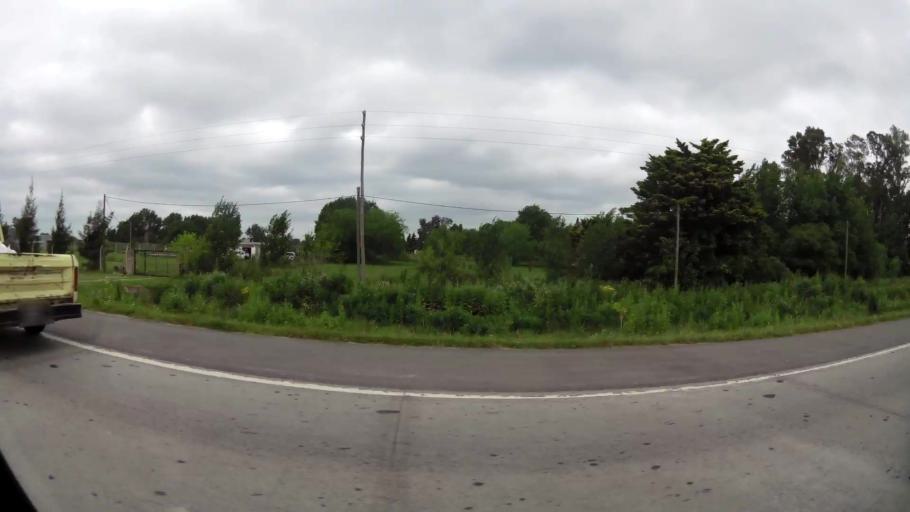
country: AR
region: Buenos Aires
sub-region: Partido de San Vicente
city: San Vicente
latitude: -35.0471
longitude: -58.4217
